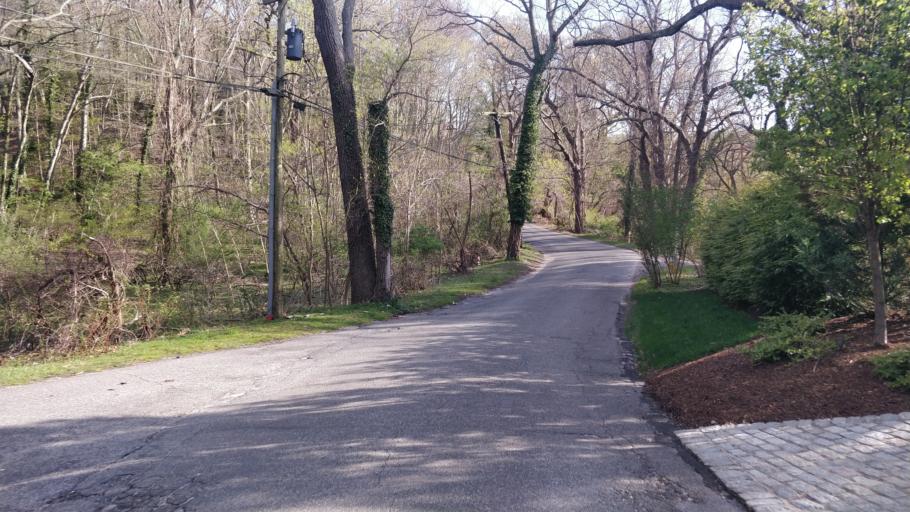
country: US
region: New York
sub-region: Suffolk County
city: Head of the Harbor
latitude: 40.8992
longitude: -73.1673
